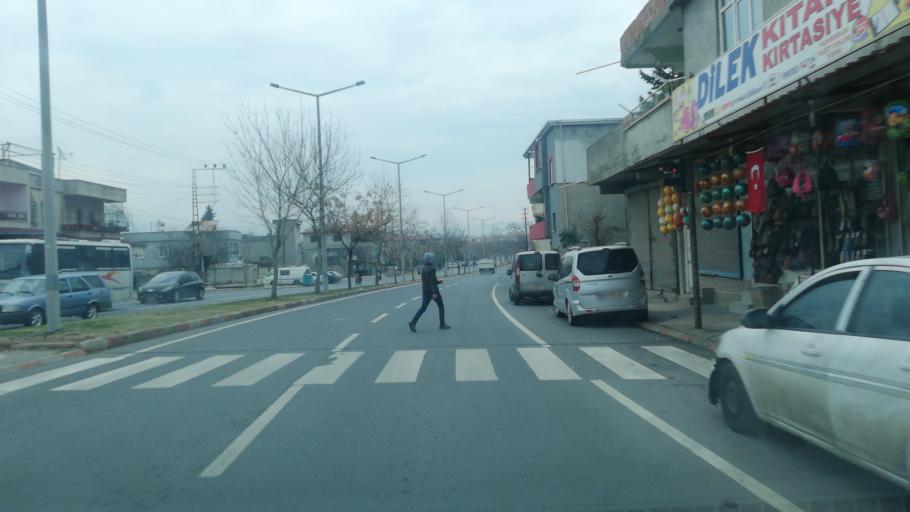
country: TR
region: Kahramanmaras
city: Kahramanmaras
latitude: 37.5718
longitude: 36.9551
